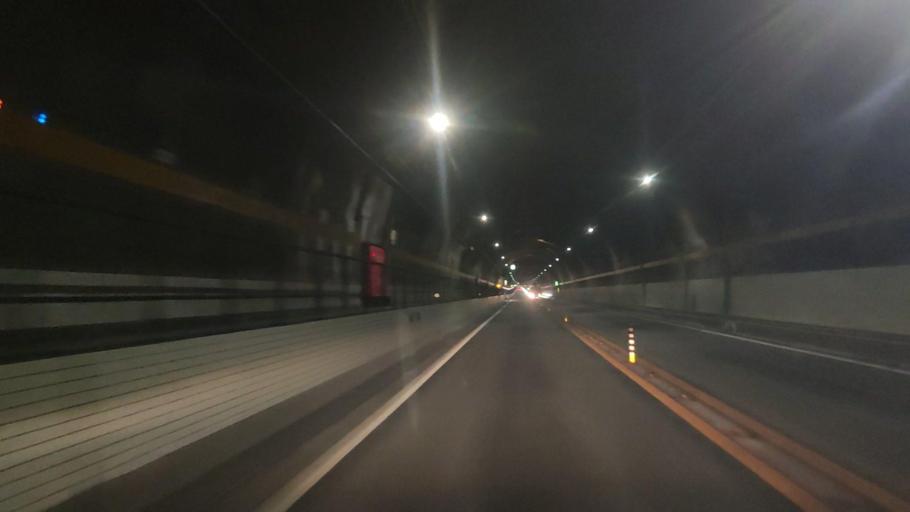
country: JP
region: Nagasaki
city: Obita
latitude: 32.7885
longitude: 129.8820
